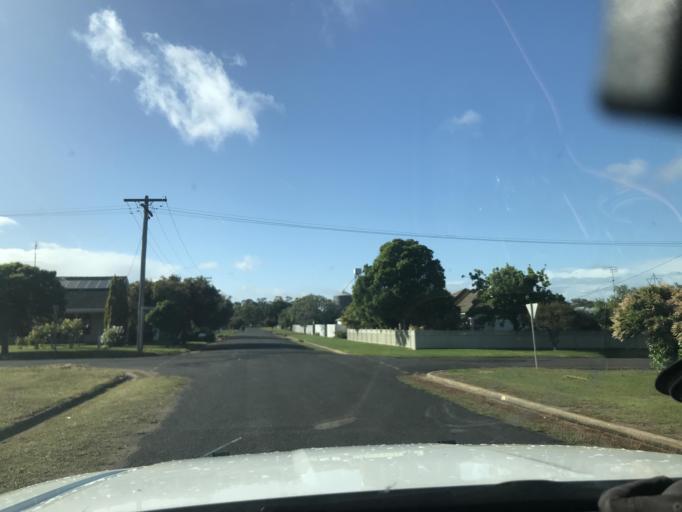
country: AU
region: Victoria
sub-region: Horsham
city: Horsham
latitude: -36.7194
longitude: 141.4727
